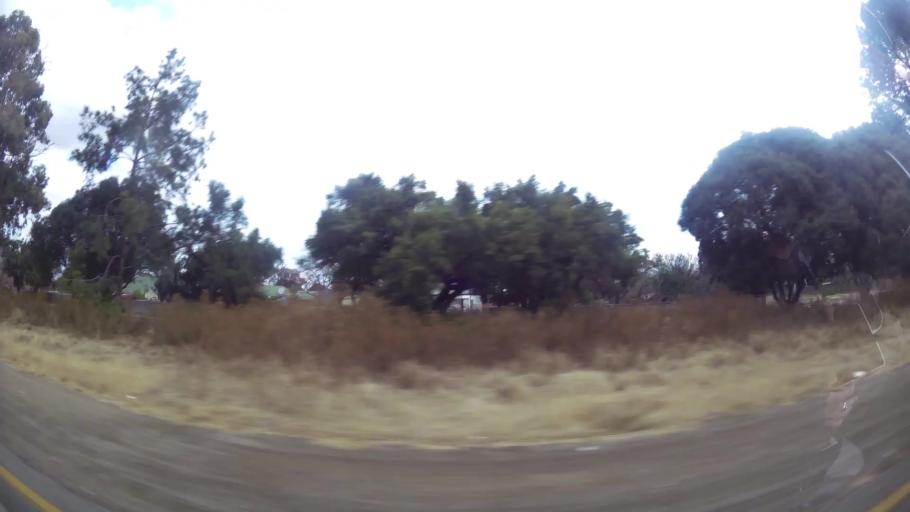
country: ZA
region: Orange Free State
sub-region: Fezile Dabi District Municipality
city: Sasolburg
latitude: -26.8103
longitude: 27.8384
